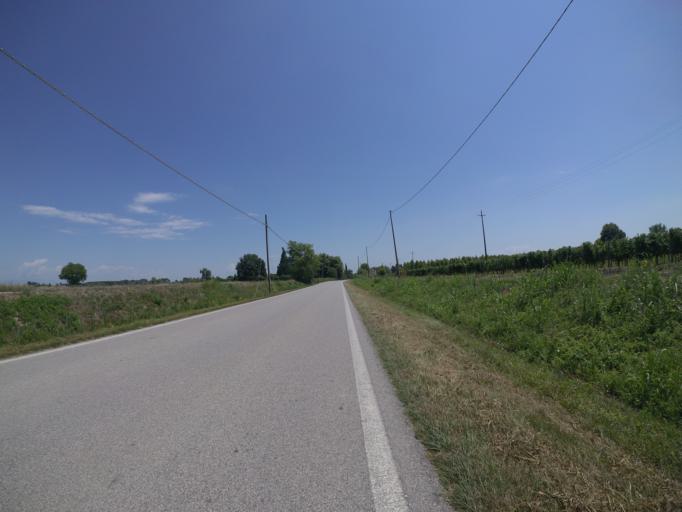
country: IT
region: Friuli Venezia Giulia
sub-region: Provincia di Udine
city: Pocenia
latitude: 45.8694
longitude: 13.0984
